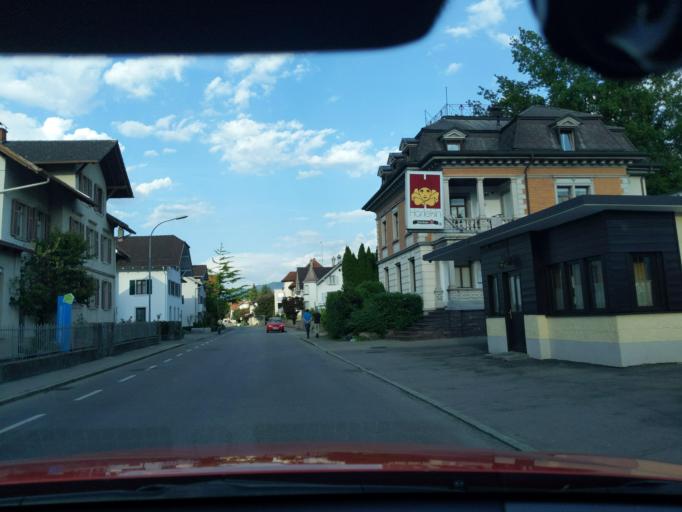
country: AT
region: Vorarlberg
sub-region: Politischer Bezirk Dornbirn
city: Lustenau
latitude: 47.4315
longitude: 9.6557
